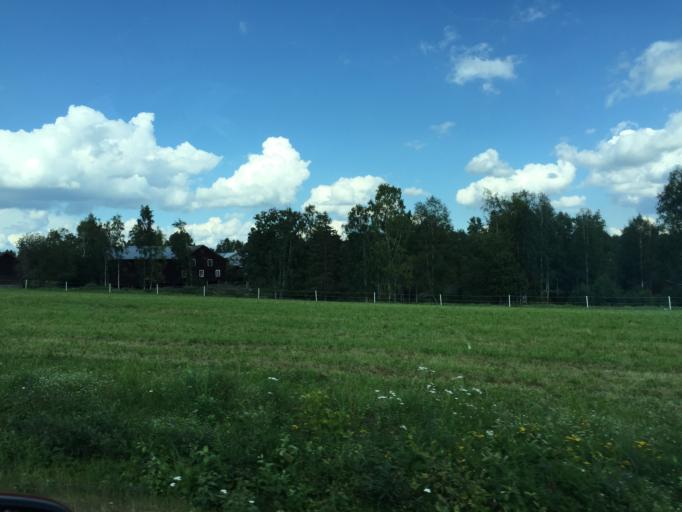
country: SE
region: Gaevleborg
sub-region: Bollnas Kommun
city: Arbra
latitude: 61.4571
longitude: 16.3760
